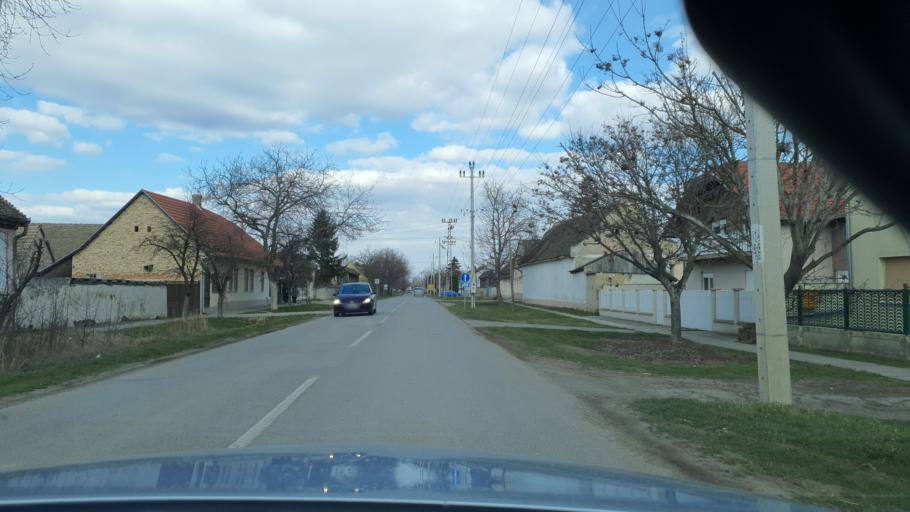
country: RS
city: Ravno Selo
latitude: 45.4492
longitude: 19.6107
